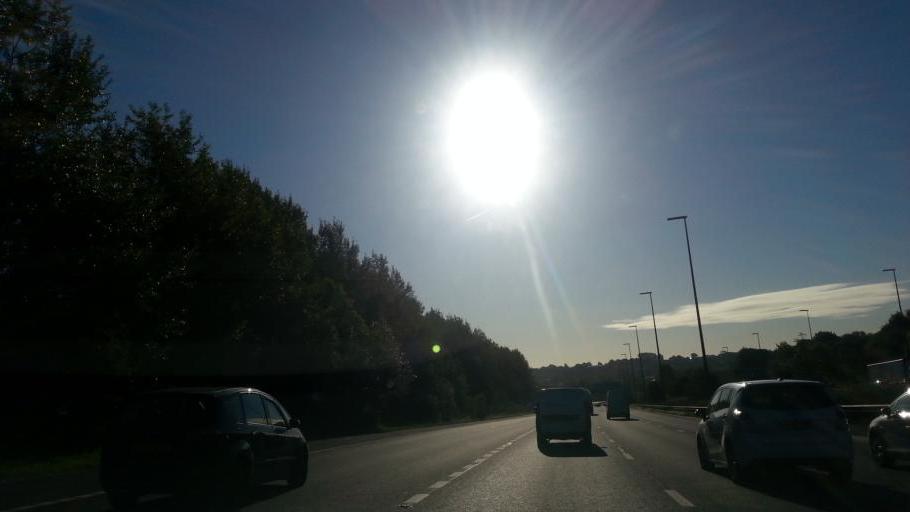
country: GB
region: England
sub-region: Manchester
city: Crumpsall
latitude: 53.5437
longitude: -2.2455
